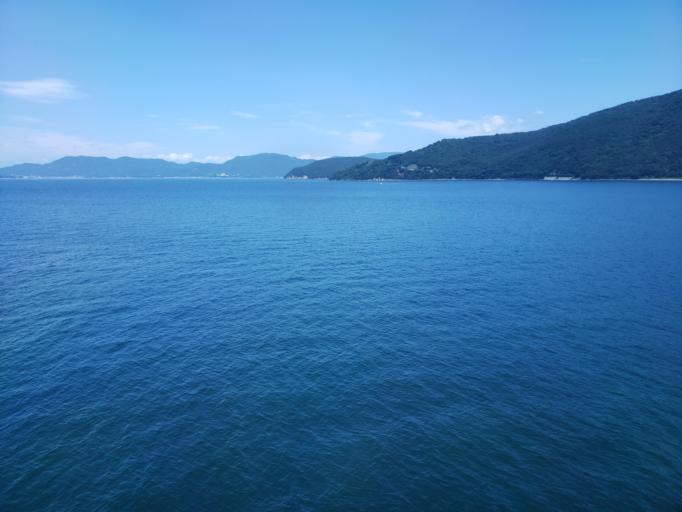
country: JP
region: Kagawa
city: Tonosho
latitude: 34.4073
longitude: 134.2217
